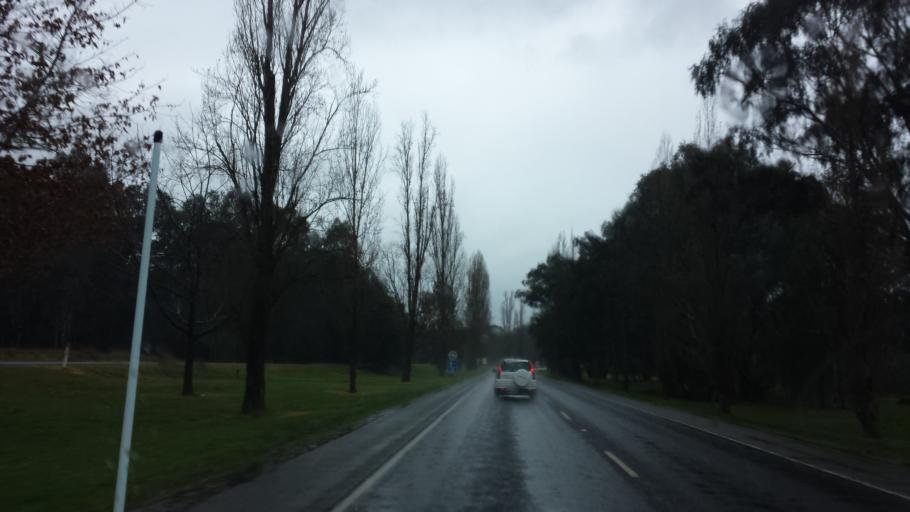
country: AU
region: Victoria
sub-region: Wangaratta
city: Wangaratta
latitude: -36.5526
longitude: 146.7045
